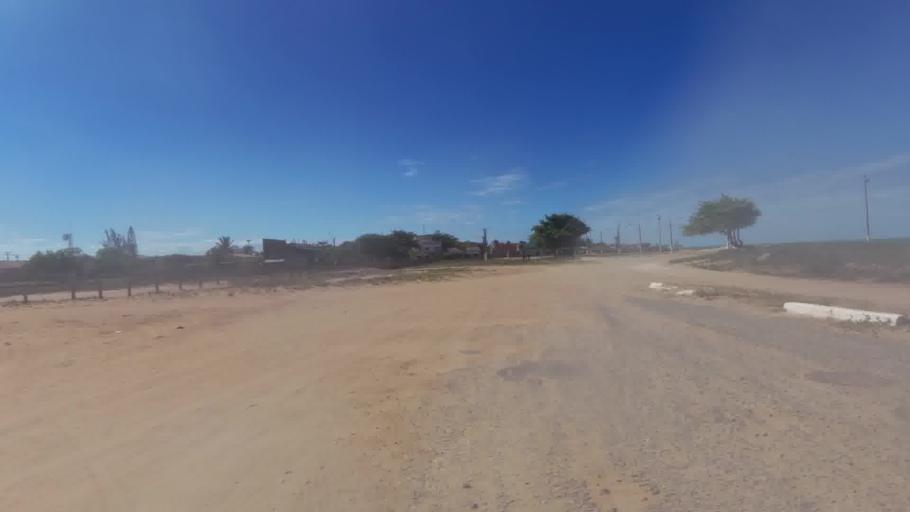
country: BR
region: Espirito Santo
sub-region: Marataizes
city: Marataizes
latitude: -21.1927
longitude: -40.9294
